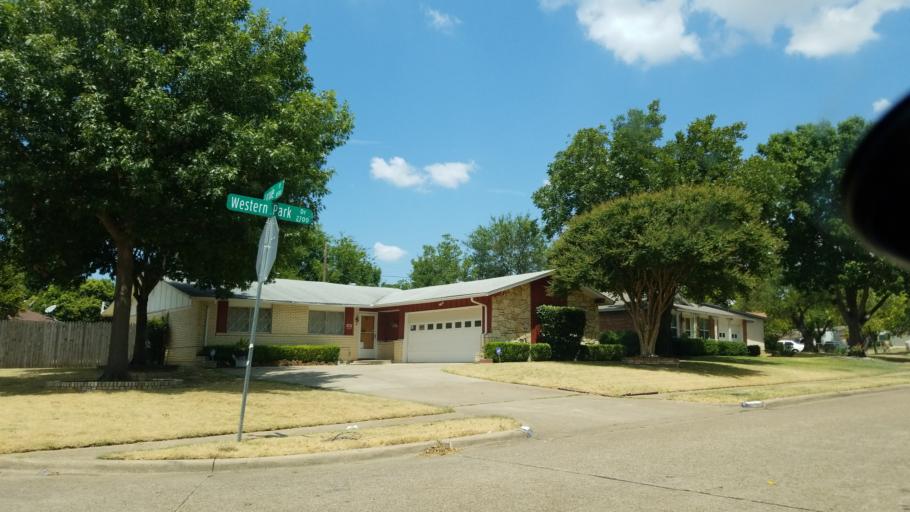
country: US
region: Texas
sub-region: Dallas County
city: Cockrell Hill
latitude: 32.7134
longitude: -96.8929
